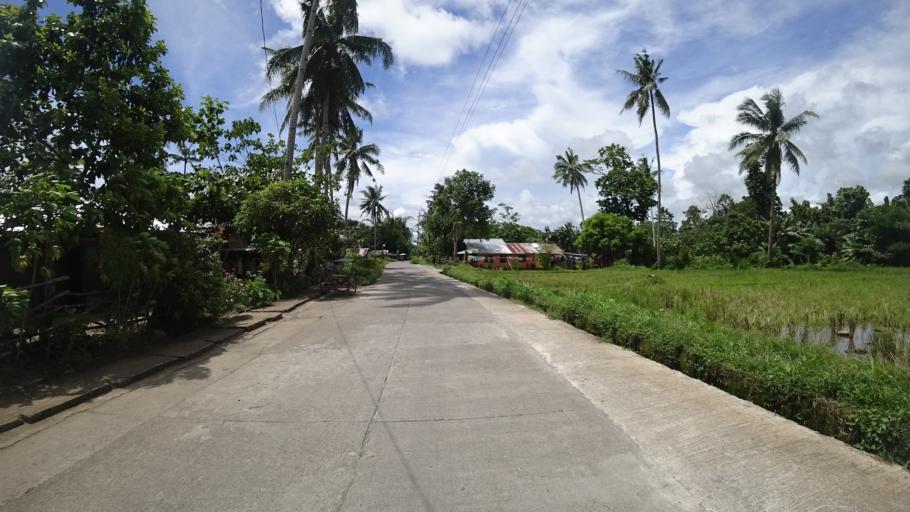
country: PH
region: Eastern Visayas
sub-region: Province of Leyte
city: Alangalang
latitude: 11.2115
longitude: 124.8455
